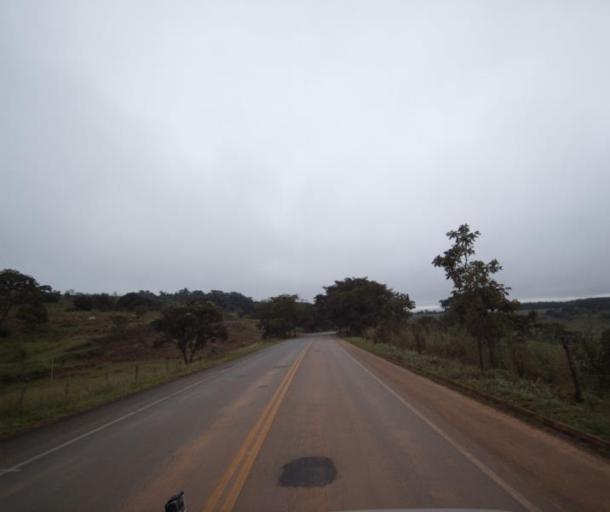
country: BR
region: Goias
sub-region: Pirenopolis
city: Pirenopolis
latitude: -15.9634
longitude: -48.8197
